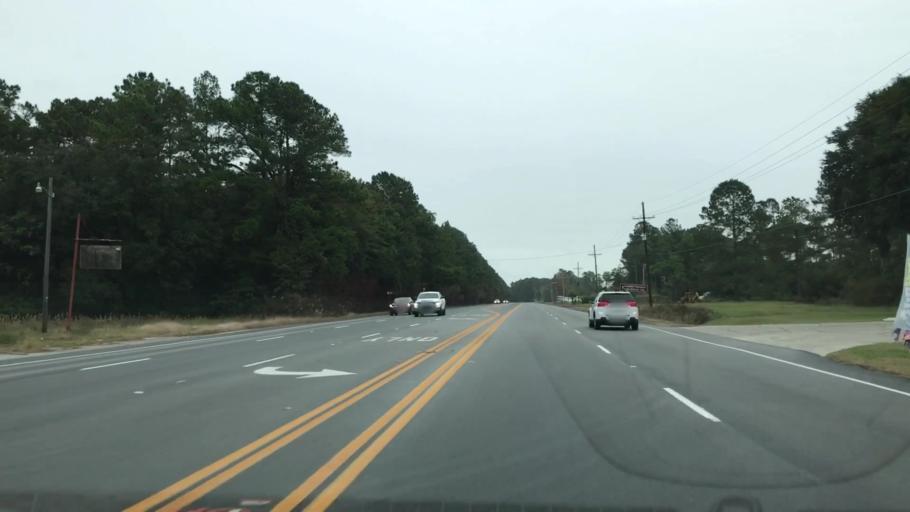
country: US
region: South Carolina
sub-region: Charleston County
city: Awendaw
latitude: 33.0954
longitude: -79.4760
